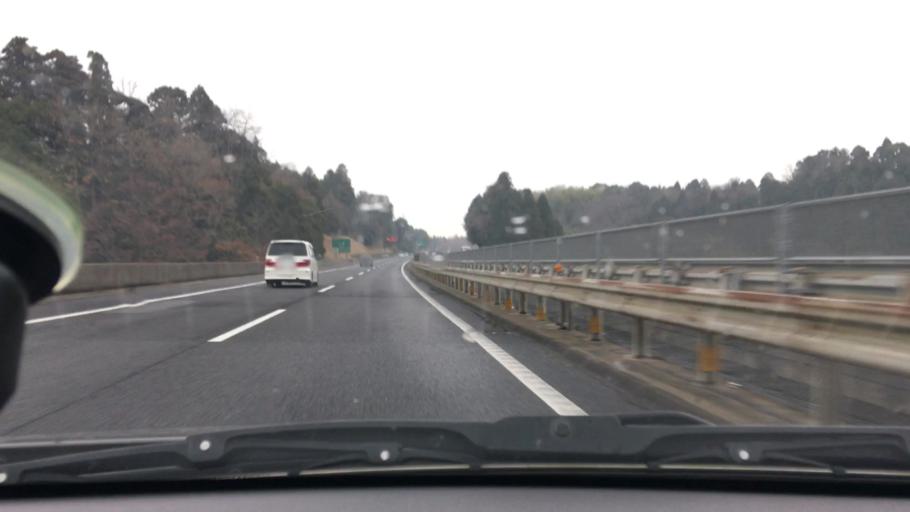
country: JP
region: Chiba
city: Sawara
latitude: 35.8339
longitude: 140.4424
